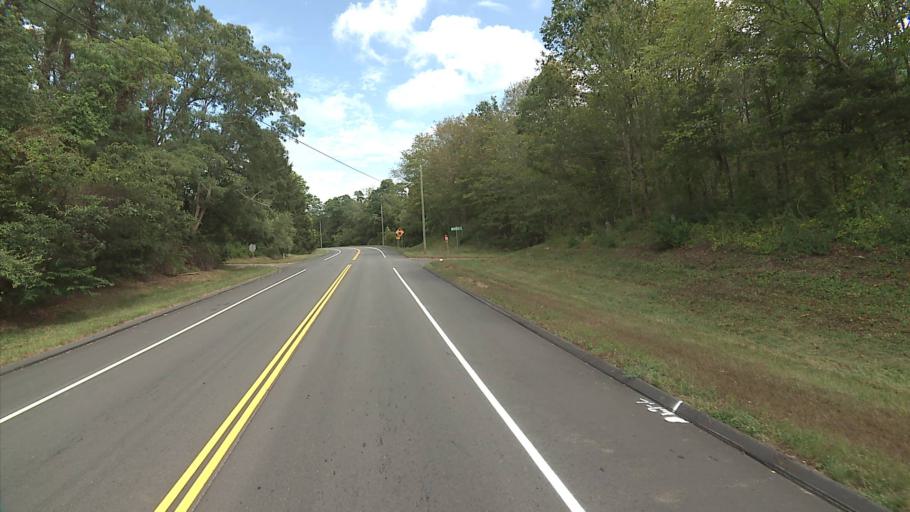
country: US
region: Connecticut
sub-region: New London County
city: Colchester
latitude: 41.5609
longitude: -72.3174
